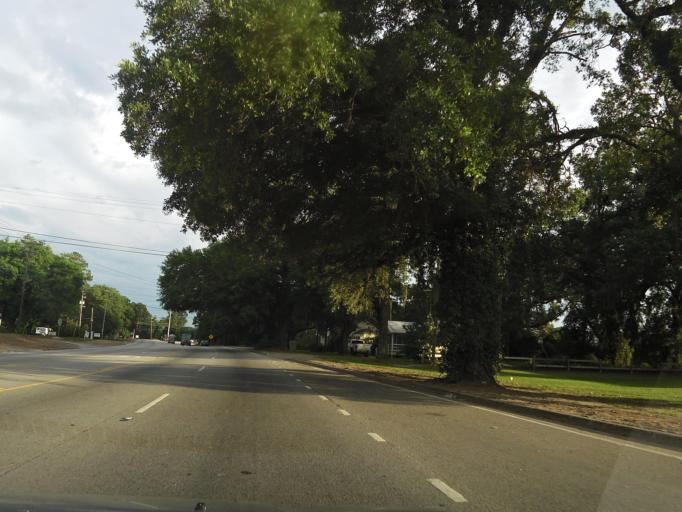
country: US
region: Georgia
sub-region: Chatham County
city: Garden City
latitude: 32.0851
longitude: -81.1972
